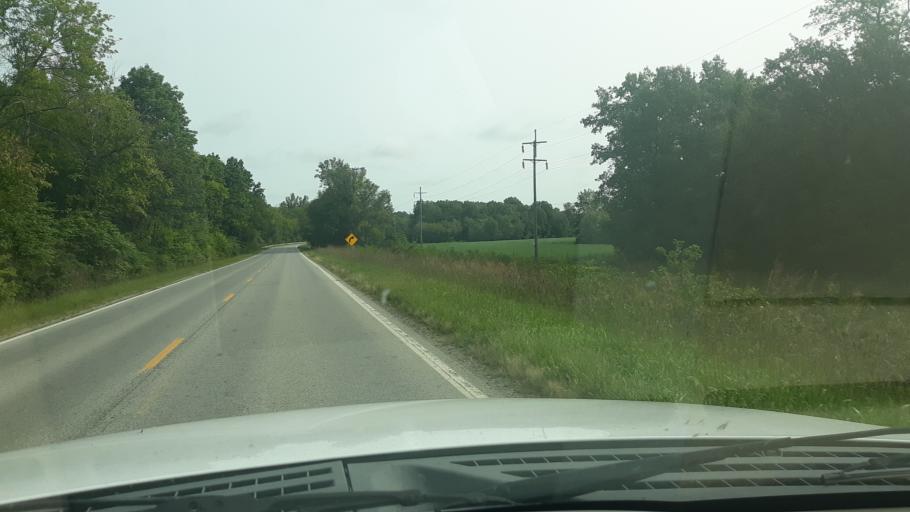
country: US
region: Illinois
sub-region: Saline County
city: Eldorado
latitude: 37.8889
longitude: -88.3841
